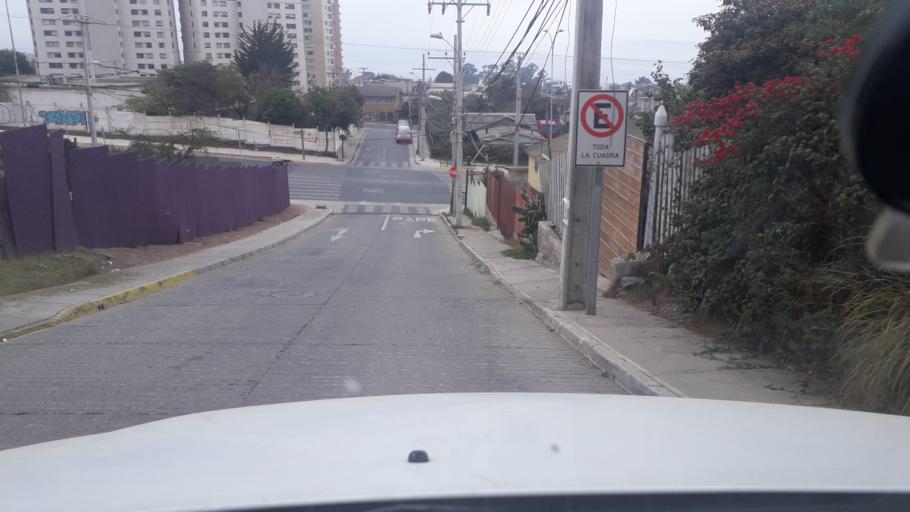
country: CL
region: Valparaiso
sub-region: Provincia de Valparaiso
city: Vina del Mar
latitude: -32.9375
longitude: -71.5333
